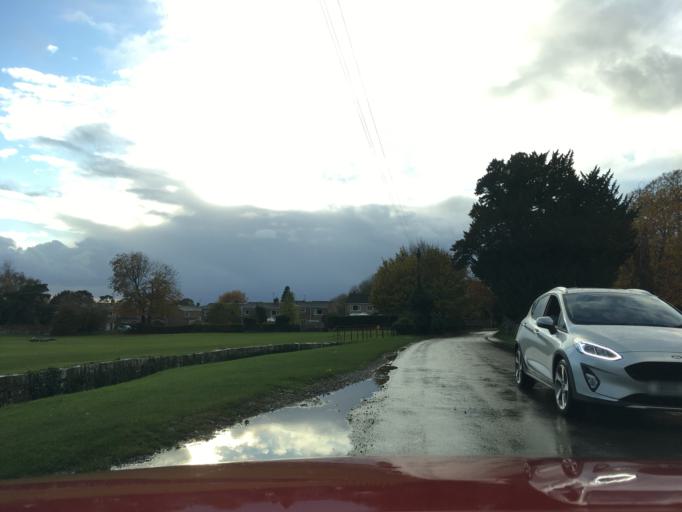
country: GB
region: England
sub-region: South Gloucestershire
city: Almondsbury
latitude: 51.5768
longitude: -2.5618
